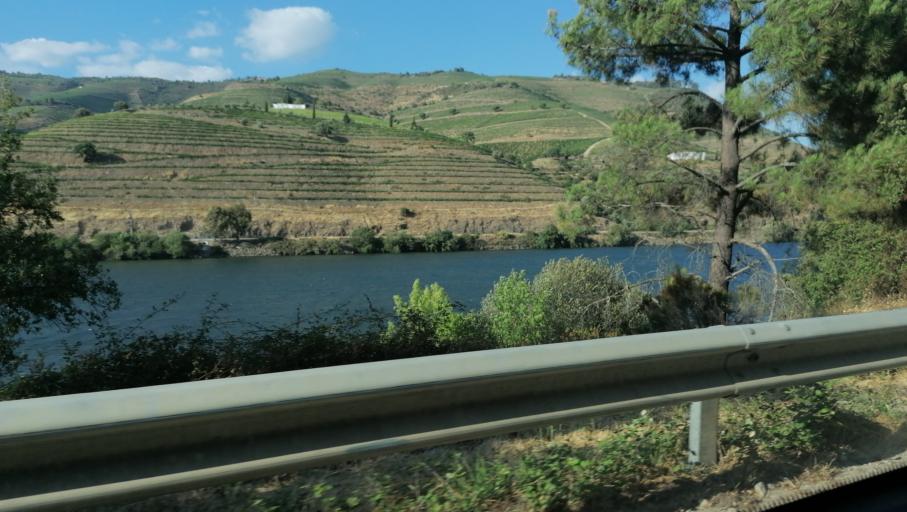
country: PT
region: Viseu
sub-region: Tabuaco
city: Tabuaco
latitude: 41.1561
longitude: -7.5997
